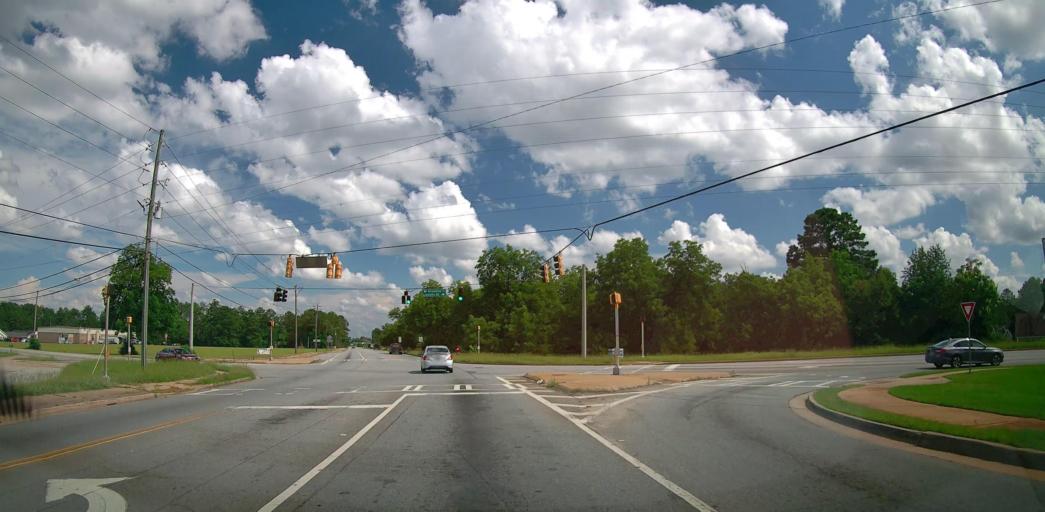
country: US
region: Georgia
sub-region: Houston County
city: Centerville
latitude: 32.6016
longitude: -83.6609
